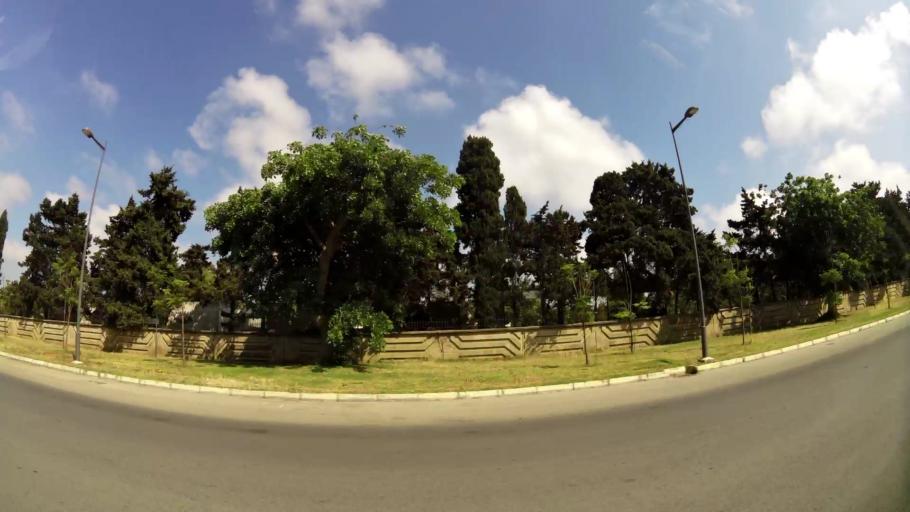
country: MA
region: Rabat-Sale-Zemmour-Zaer
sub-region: Rabat
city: Rabat
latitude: 33.9795
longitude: -6.8661
